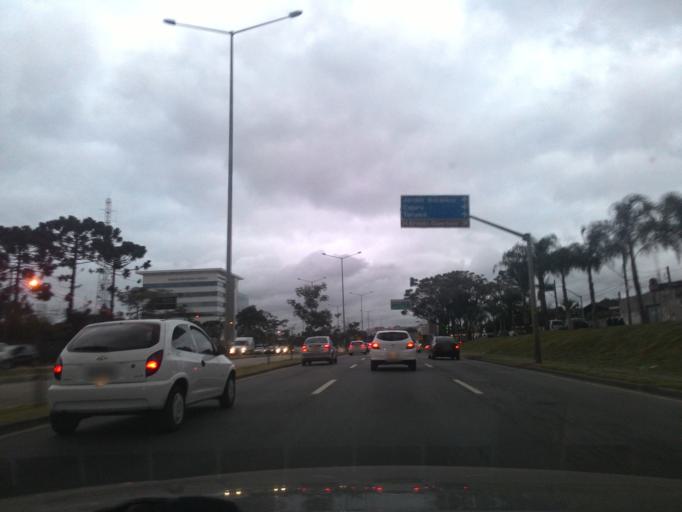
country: BR
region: Parana
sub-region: Curitiba
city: Curitiba
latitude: -25.4542
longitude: -49.2465
